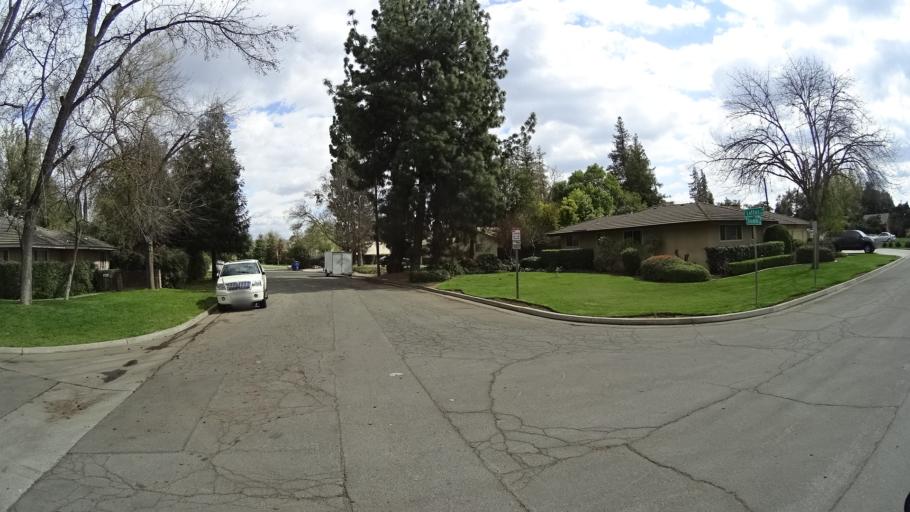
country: US
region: California
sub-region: Fresno County
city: Clovis
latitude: 36.8179
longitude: -119.7617
